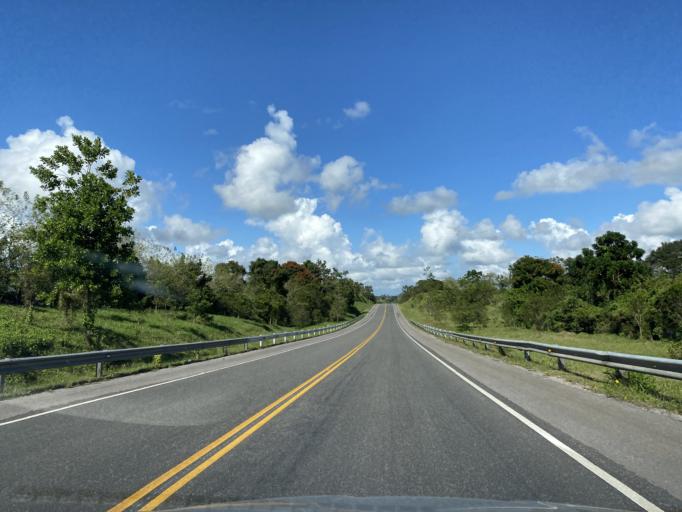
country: DO
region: Monte Plata
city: Majagual
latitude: 19.0151
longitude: -69.8229
